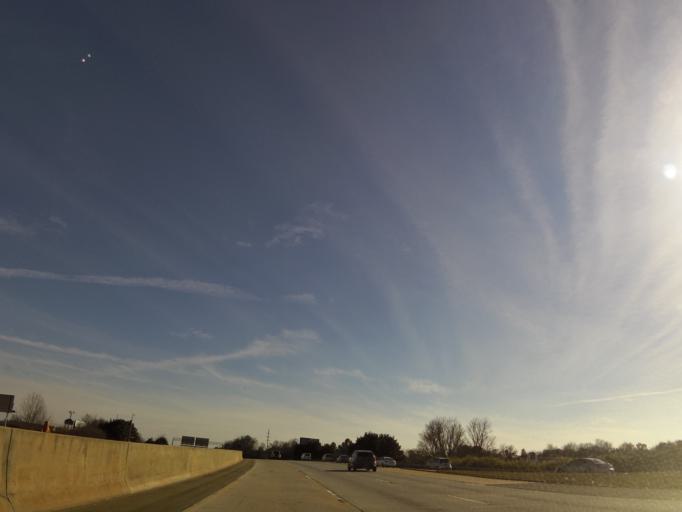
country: US
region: Georgia
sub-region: Muscogee County
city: Columbus
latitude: 32.5079
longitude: -84.9506
